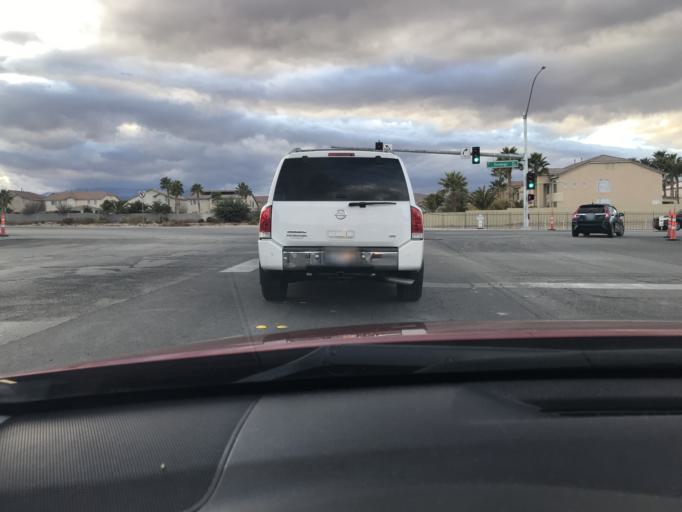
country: US
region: Nevada
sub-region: Clark County
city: Enterprise
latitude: 36.0409
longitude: -115.2787
